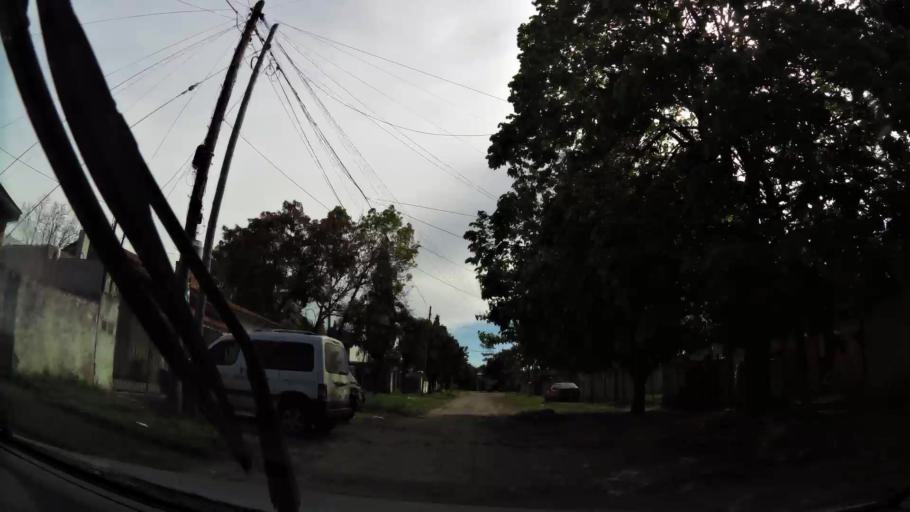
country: AR
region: Buenos Aires
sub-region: Partido de Almirante Brown
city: Adrogue
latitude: -34.8032
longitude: -58.3452
